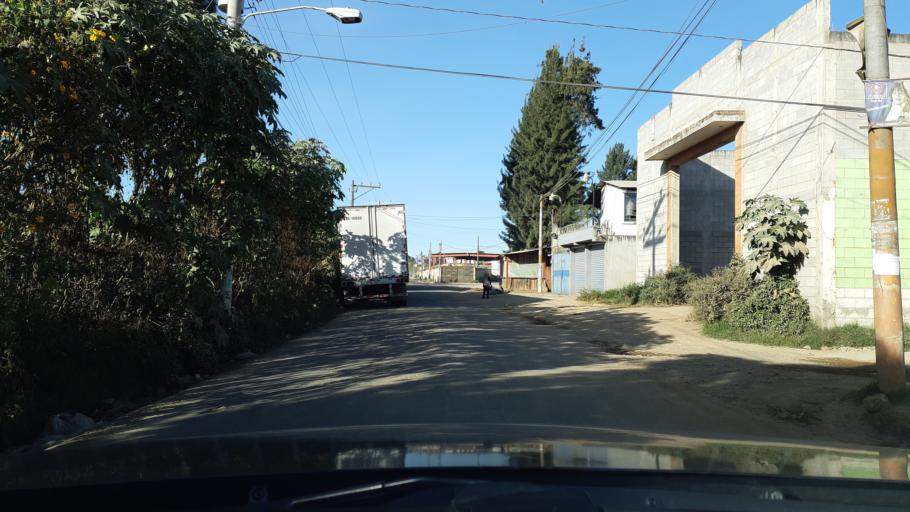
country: GT
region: Chimaltenango
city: El Tejar
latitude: 14.6409
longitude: -90.7993
